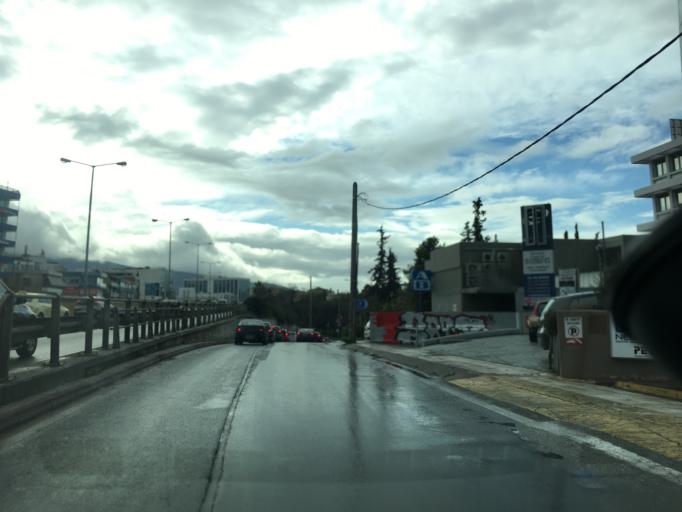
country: GR
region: Attica
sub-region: Nomarchia Athinas
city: Filothei
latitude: 38.0251
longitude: 23.7894
